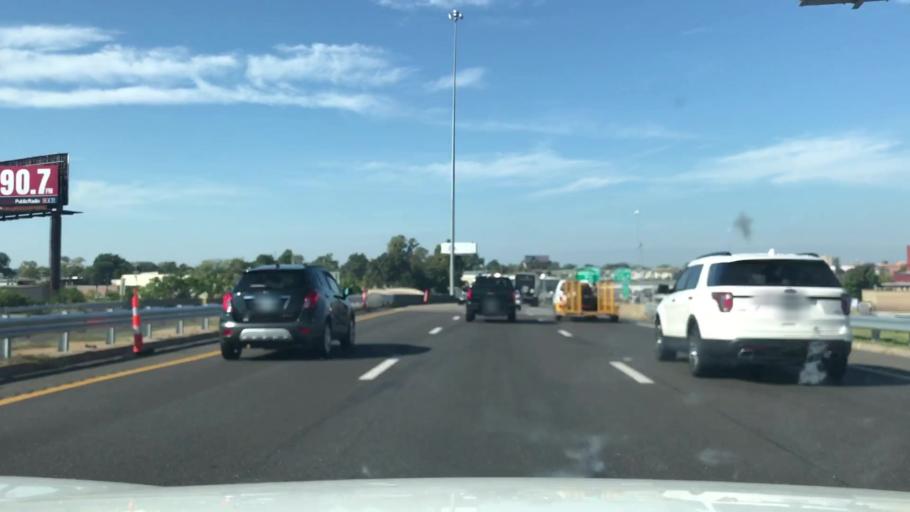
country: US
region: Missouri
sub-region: City of Saint Louis
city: St. Louis
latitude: 38.6315
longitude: -90.2483
